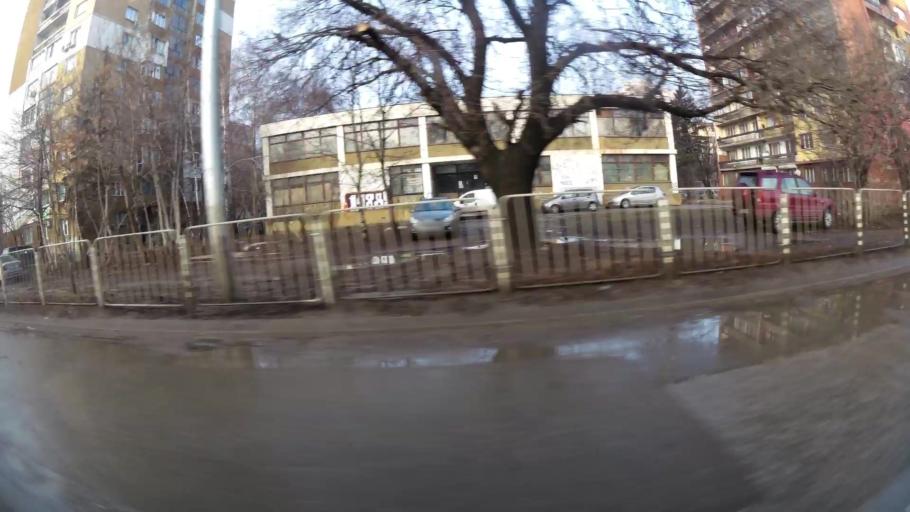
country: BG
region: Sofia-Capital
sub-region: Stolichna Obshtina
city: Sofia
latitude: 42.7259
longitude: 23.3120
